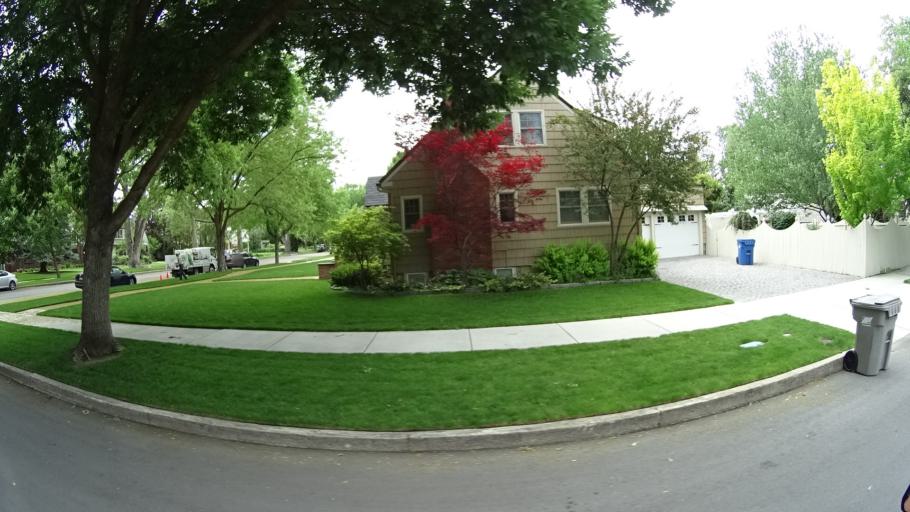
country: US
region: Idaho
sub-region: Ada County
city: Garden City
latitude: 43.6312
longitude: -116.2186
